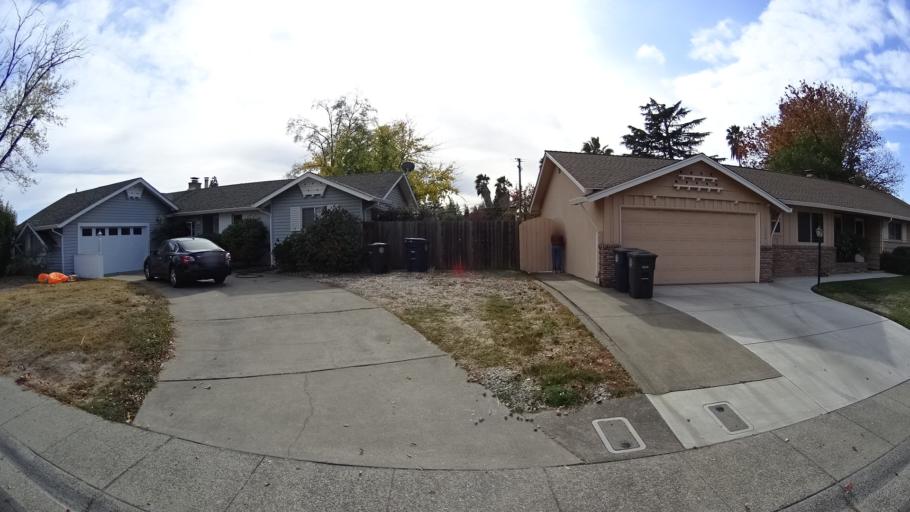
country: US
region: California
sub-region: Sacramento County
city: Fair Oaks
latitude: 38.6648
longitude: -121.2789
